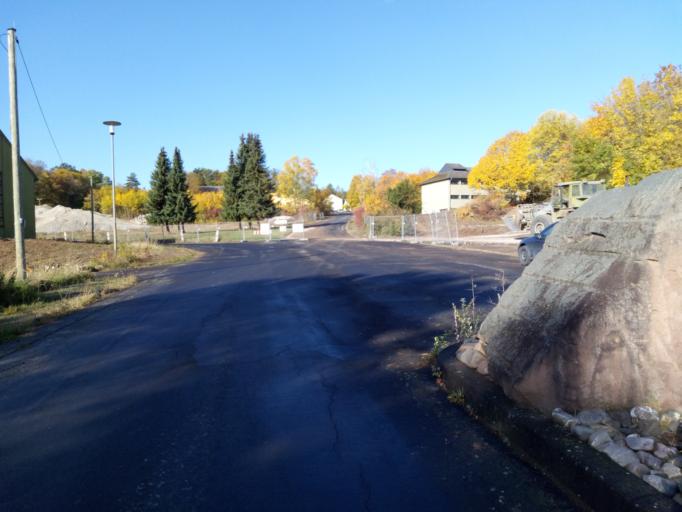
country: DE
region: Rheinland-Pfalz
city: Nussbaum
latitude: 49.8077
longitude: 7.6386
